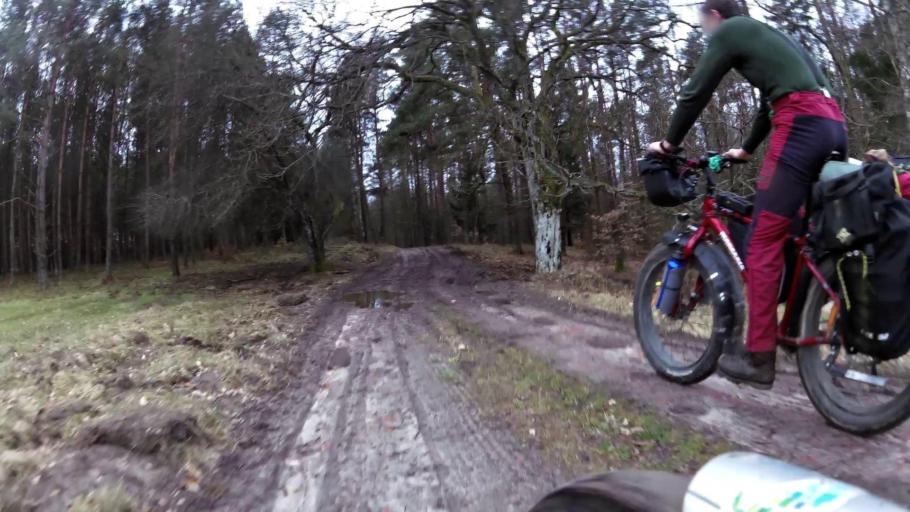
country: PL
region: Pomeranian Voivodeship
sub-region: Powiat bytowski
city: Trzebielino
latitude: 54.1352
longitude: 17.1445
